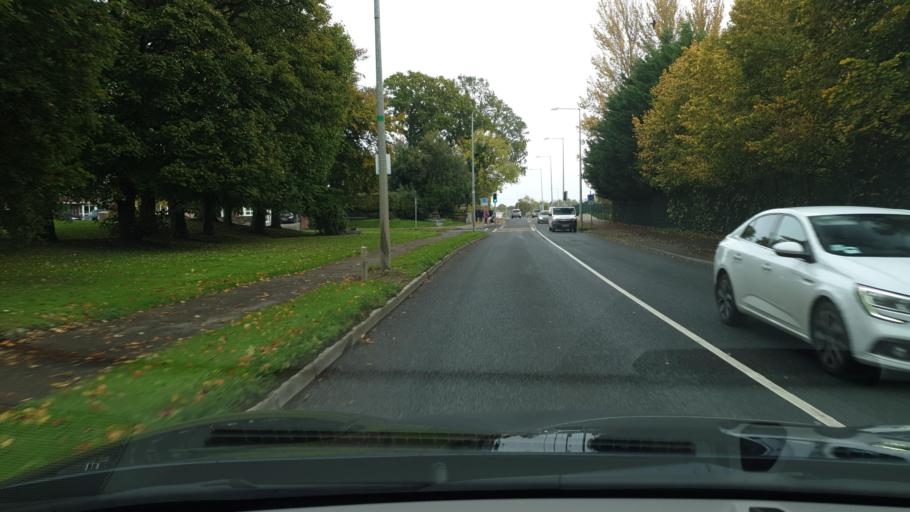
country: IE
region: Leinster
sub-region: An Mhi
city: Ratoath
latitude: 53.5053
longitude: -6.4540
